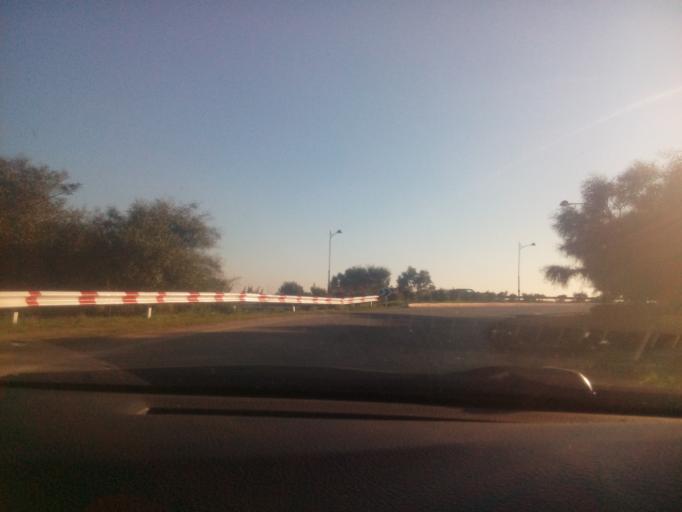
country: DZ
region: Oran
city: Bir el Djir
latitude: 35.7736
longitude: -0.4354
